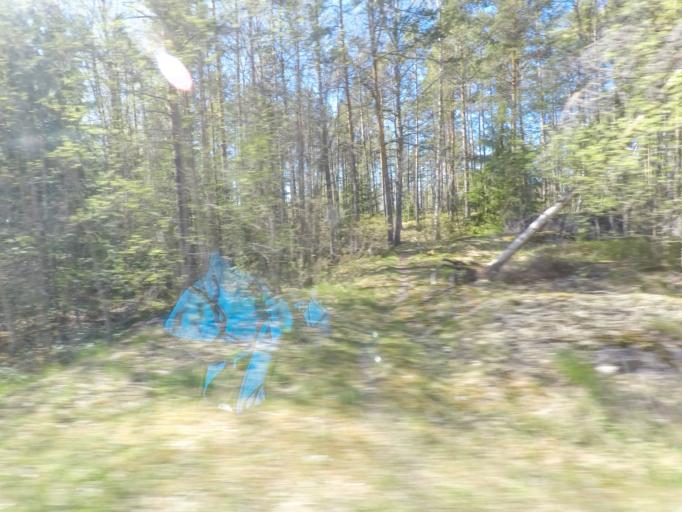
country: FI
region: Uusimaa
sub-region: Helsinki
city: Sammatti
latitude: 60.3564
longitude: 23.8021
